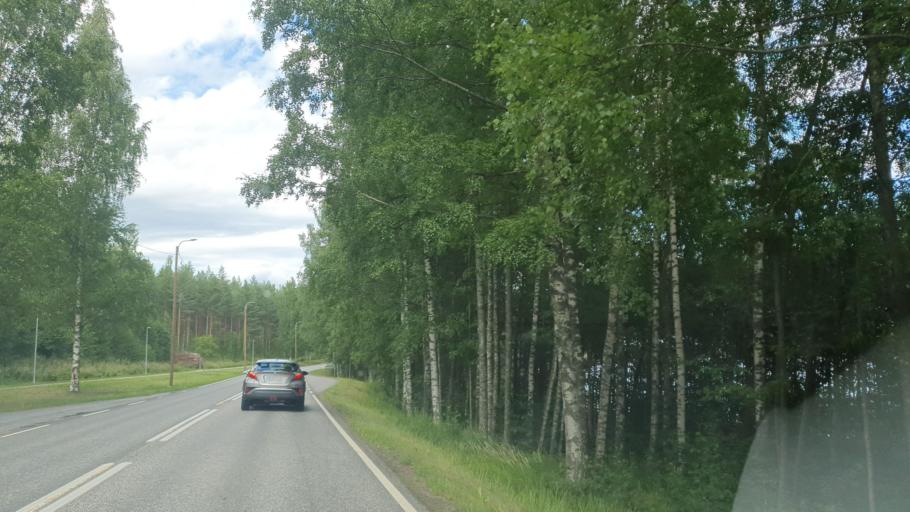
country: FI
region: Central Finland
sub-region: Jyvaeskylae
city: Saeynaetsalo
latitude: 62.1426
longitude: 25.7436
